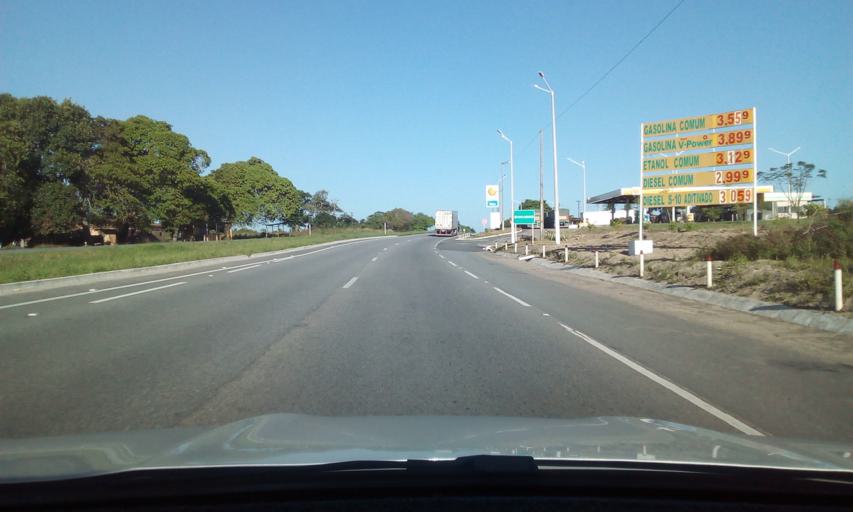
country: BR
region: Paraiba
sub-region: Pilar
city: Pilar
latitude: -7.1873
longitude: -35.2848
